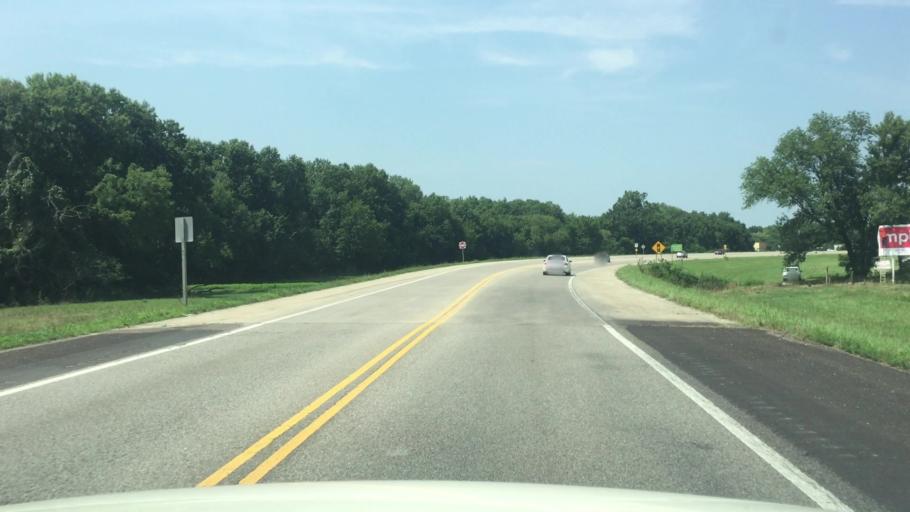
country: US
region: Kansas
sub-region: Crawford County
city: Pittsburg
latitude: 37.4065
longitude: -94.7243
